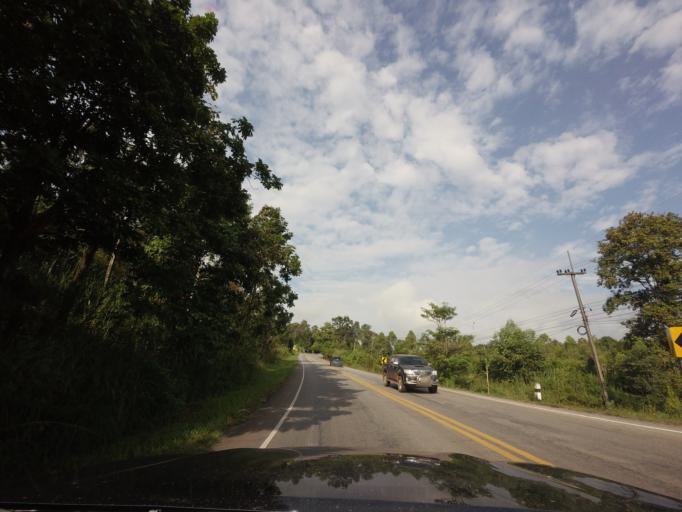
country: TH
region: Nong Khai
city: Pho Tak
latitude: 17.8074
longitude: 102.3327
